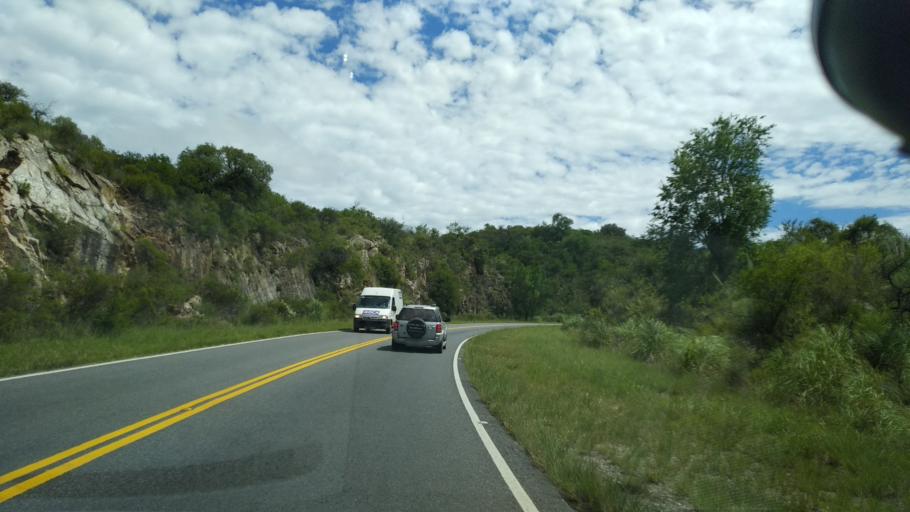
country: AR
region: Cordoba
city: Mina Clavero
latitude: -31.7567
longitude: -64.9594
